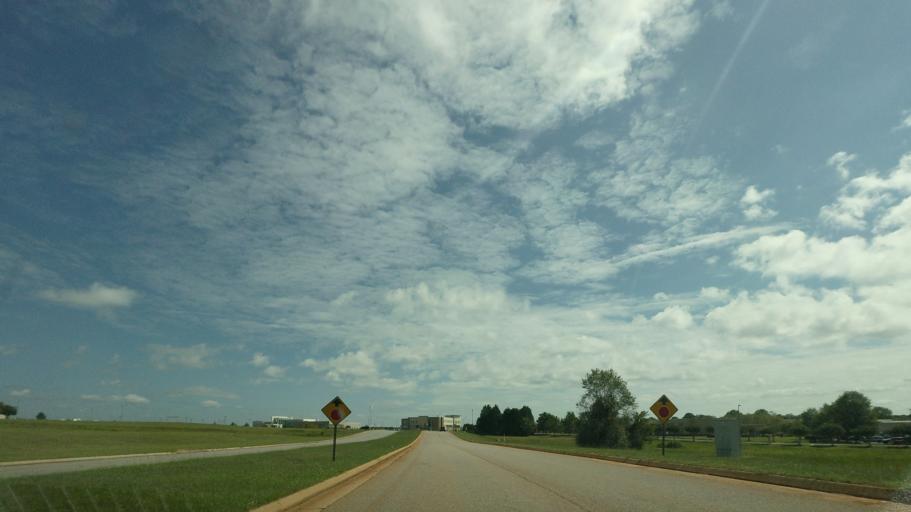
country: US
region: Georgia
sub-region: Houston County
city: Centerville
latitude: 32.5463
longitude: -83.6712
